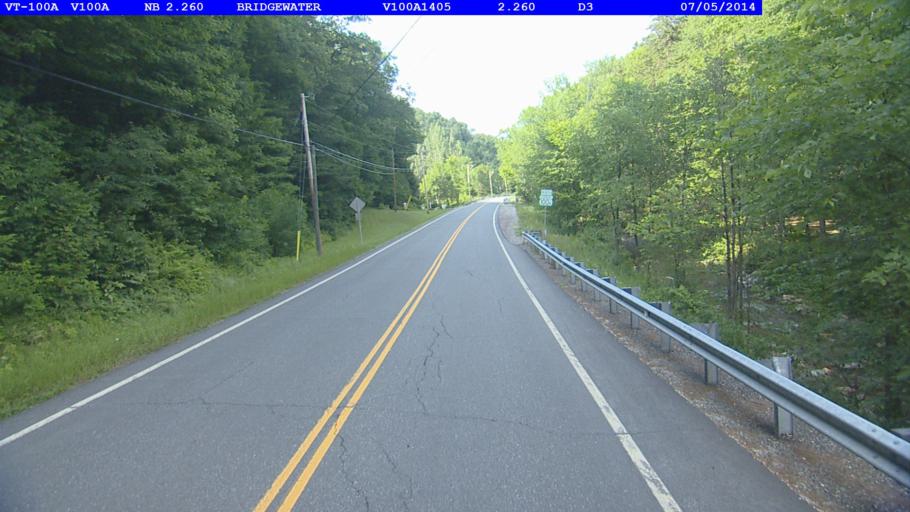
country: US
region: Vermont
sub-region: Windsor County
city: Woodstock
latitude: 43.5474
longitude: -72.7106
